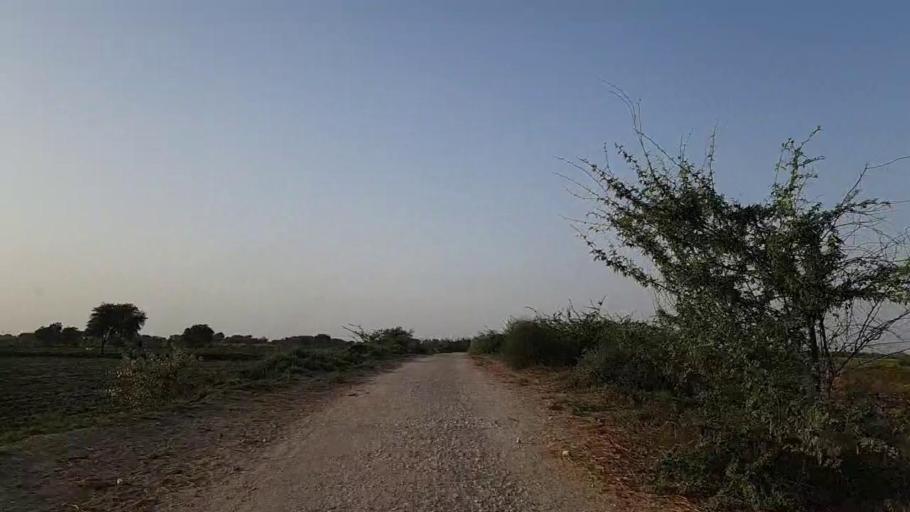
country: PK
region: Sindh
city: Jati
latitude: 24.4025
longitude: 68.1873
